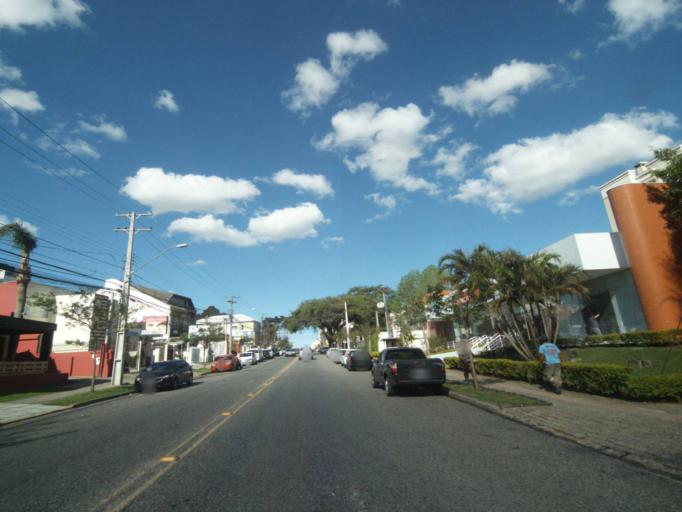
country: BR
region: Parana
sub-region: Curitiba
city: Curitiba
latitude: -25.4001
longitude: -49.2573
